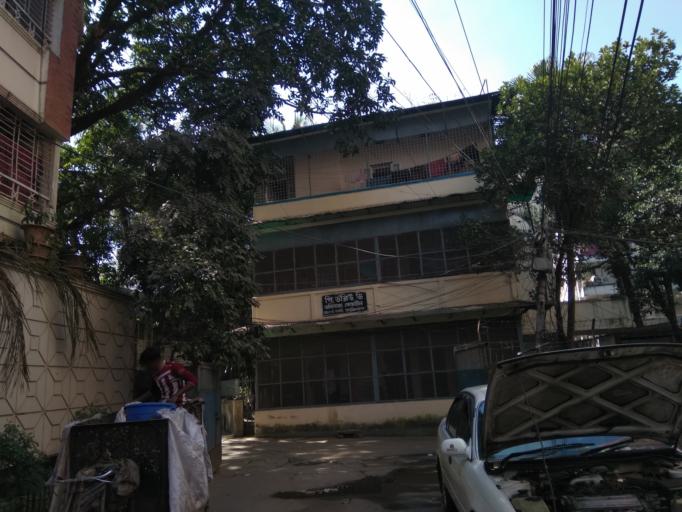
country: BD
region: Dhaka
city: Azimpur
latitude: 23.7384
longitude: 90.3754
